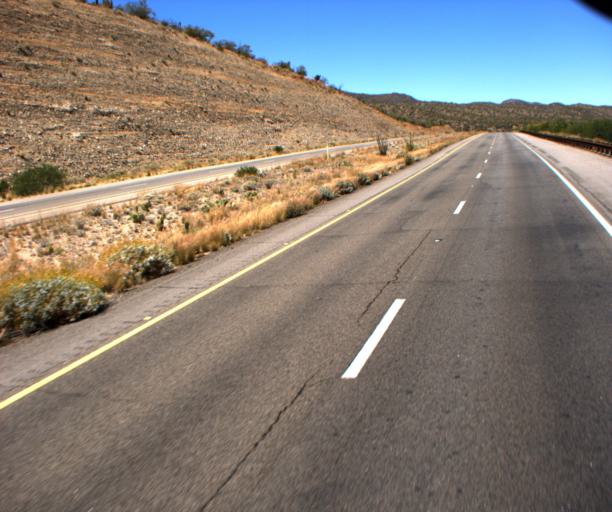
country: US
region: Arizona
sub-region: Yavapai County
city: Bagdad
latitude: 34.3859
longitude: -113.2012
